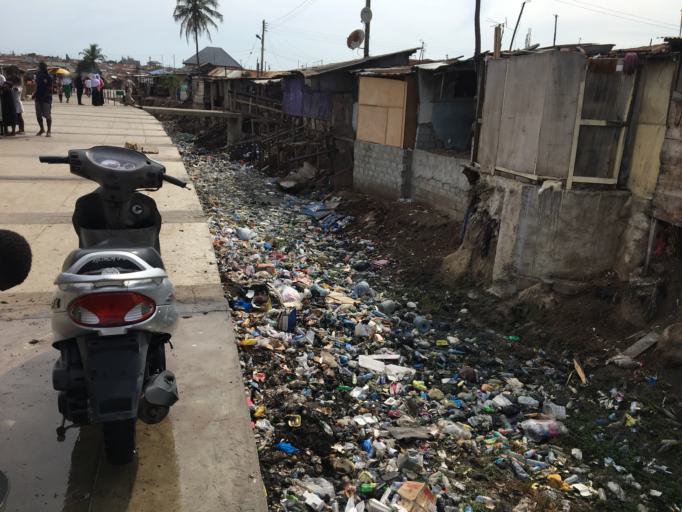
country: GH
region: Greater Accra
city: Accra
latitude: 5.5902
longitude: -0.1925
